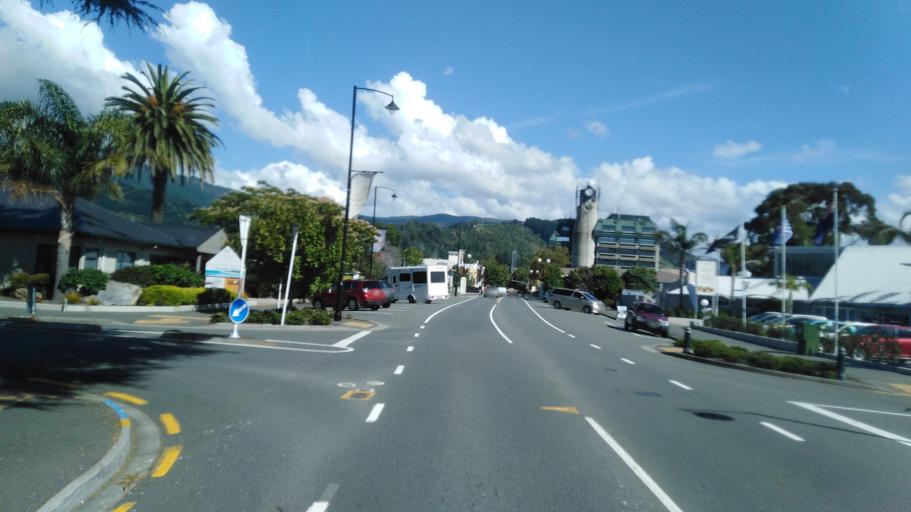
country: NZ
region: Nelson
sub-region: Nelson City
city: Nelson
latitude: -41.2689
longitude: 173.2841
